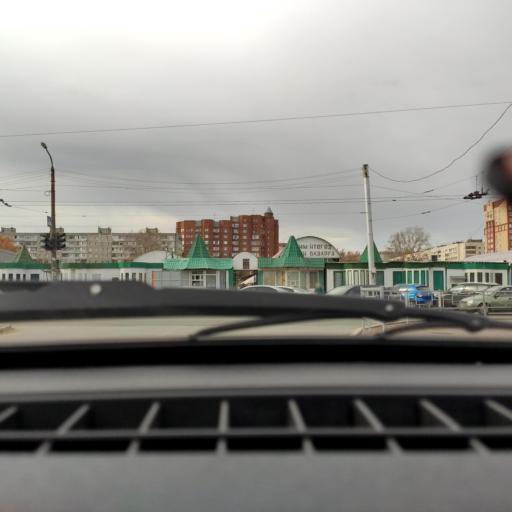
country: RU
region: Bashkortostan
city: Ufa
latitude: 54.7795
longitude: 56.1248
